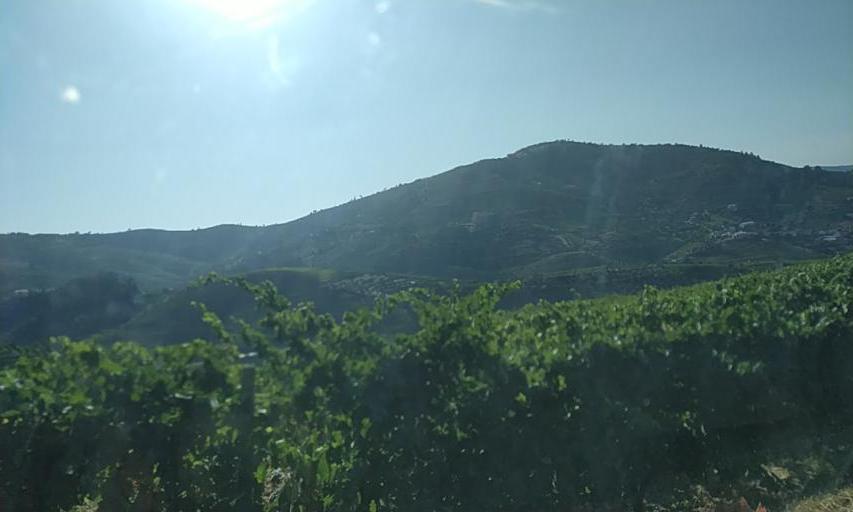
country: PT
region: Viseu
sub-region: Sao Joao da Pesqueira
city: Sao Joao da Pesqueira
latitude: 41.1735
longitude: -7.4069
